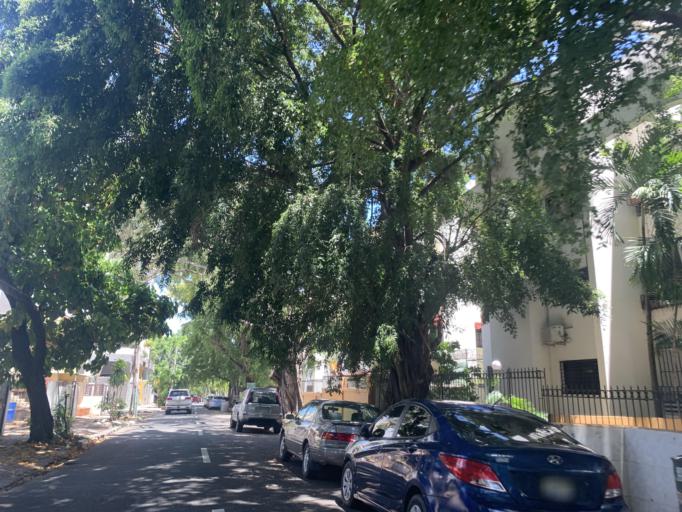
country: DO
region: Nacional
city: Ciudad Nueva
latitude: 18.4650
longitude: -69.9061
